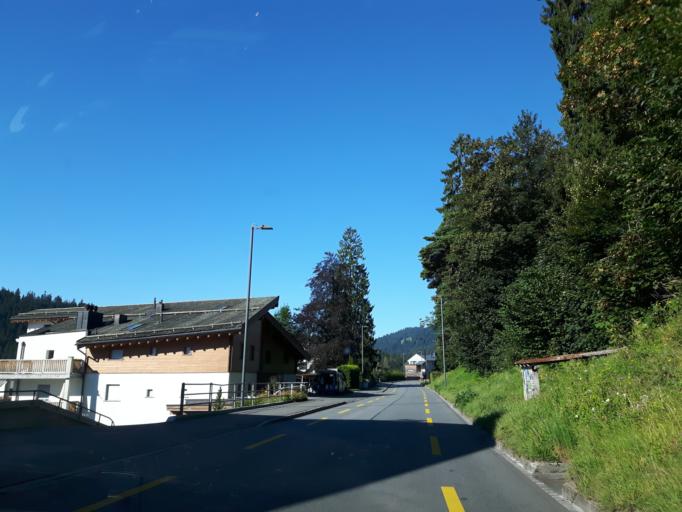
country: CH
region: Grisons
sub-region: Imboden District
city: Flims
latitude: 46.8255
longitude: 9.2873
